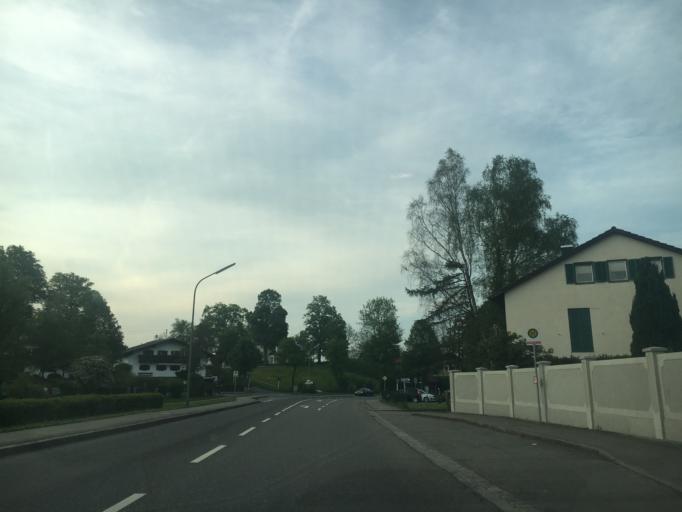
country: DE
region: Bavaria
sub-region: Upper Bavaria
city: Kochel
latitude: 47.6551
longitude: 11.3632
